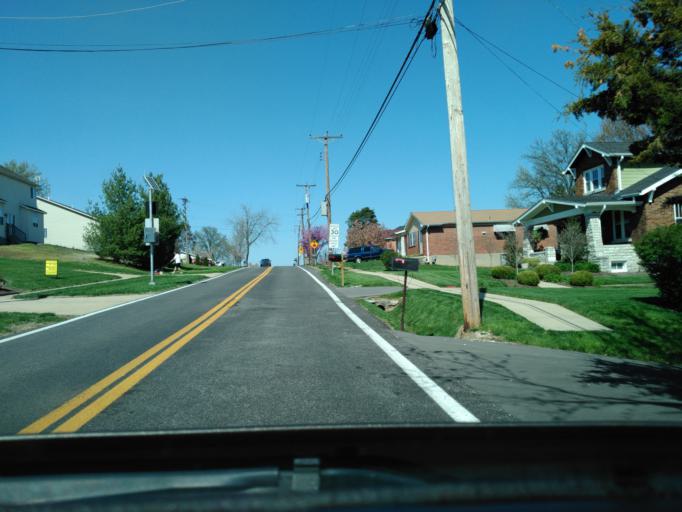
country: US
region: Missouri
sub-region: Saint Louis County
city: Concord
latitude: 38.4942
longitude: -90.3667
